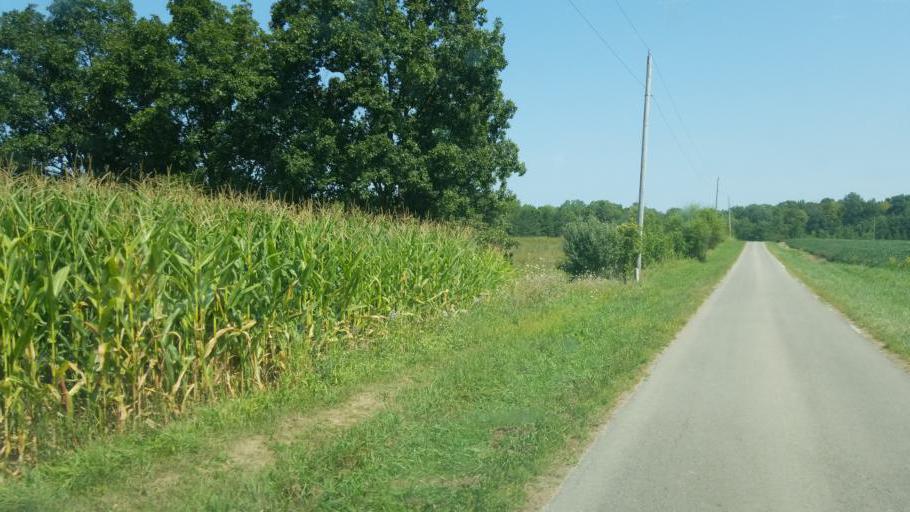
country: US
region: Ohio
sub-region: Crawford County
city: Bucyrus
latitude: 40.9330
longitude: -83.0668
